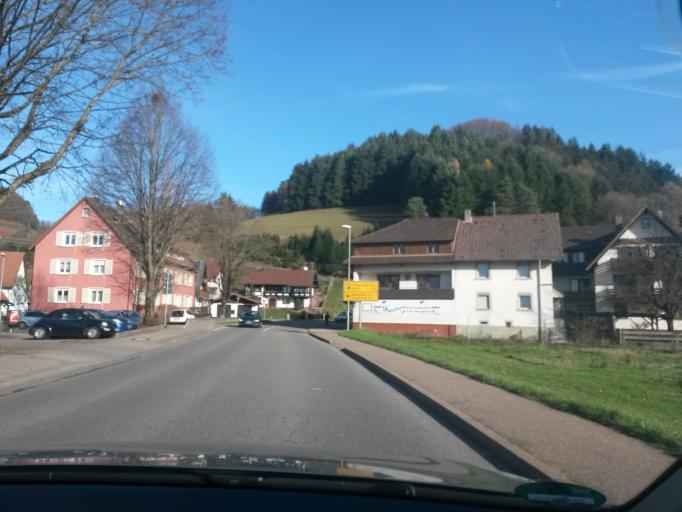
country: DE
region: Baden-Wuerttemberg
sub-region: Freiburg Region
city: Elzach
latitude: 48.1532
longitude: 8.0384
